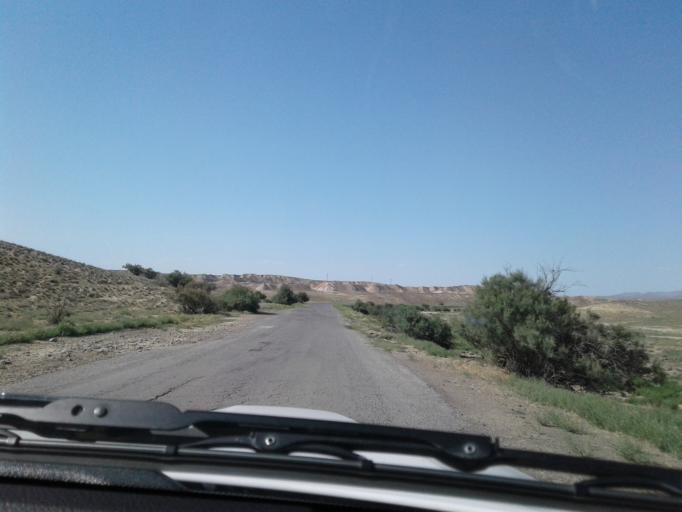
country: TM
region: Balkan
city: Magtymguly
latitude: 38.6623
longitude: 56.2856
